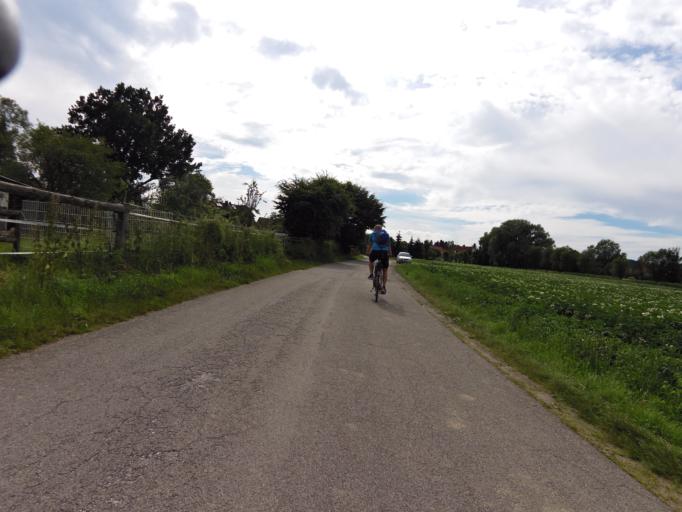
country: DE
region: Bavaria
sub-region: Upper Bavaria
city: Hebertshausen
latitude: 48.3019
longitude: 11.4948
